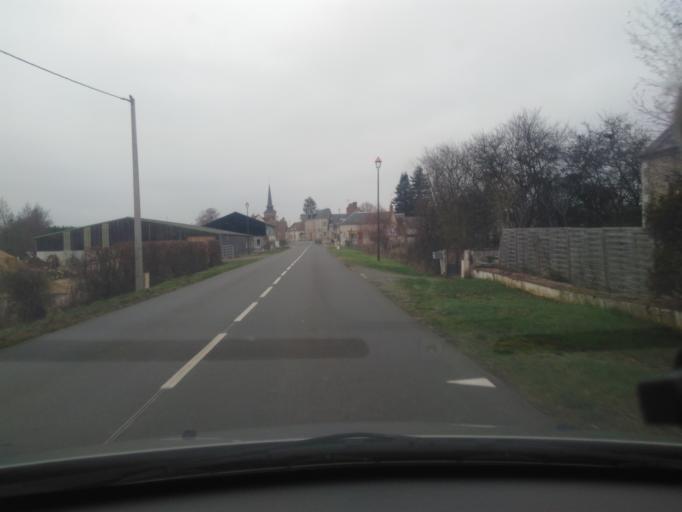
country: FR
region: Centre
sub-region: Departement du Cher
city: Le Chatelet
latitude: 46.6532
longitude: 2.3897
